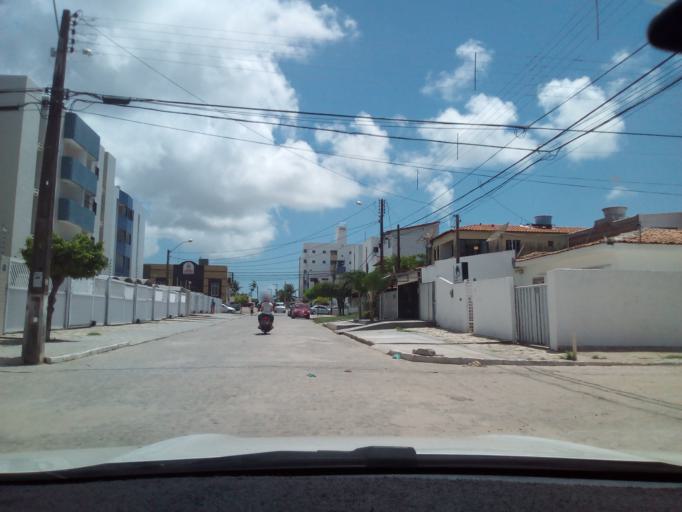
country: BR
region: Paraiba
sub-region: Joao Pessoa
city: Joao Pessoa
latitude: -7.1540
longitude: -34.8319
